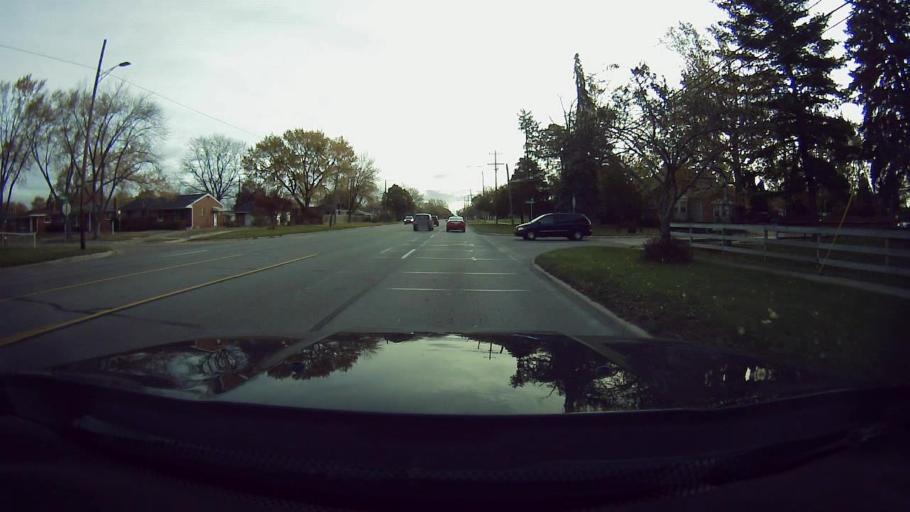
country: US
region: Michigan
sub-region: Macomb County
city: Warren
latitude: 42.4768
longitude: -83.0592
